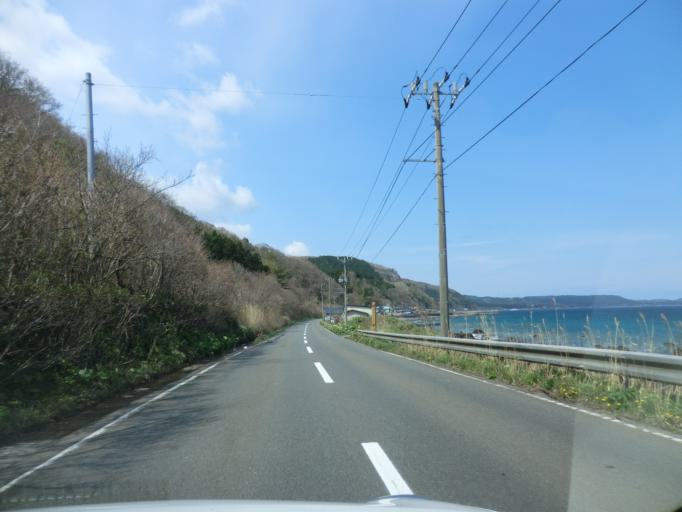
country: JP
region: Aomori
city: Mutsu
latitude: 41.4829
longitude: 141.0454
